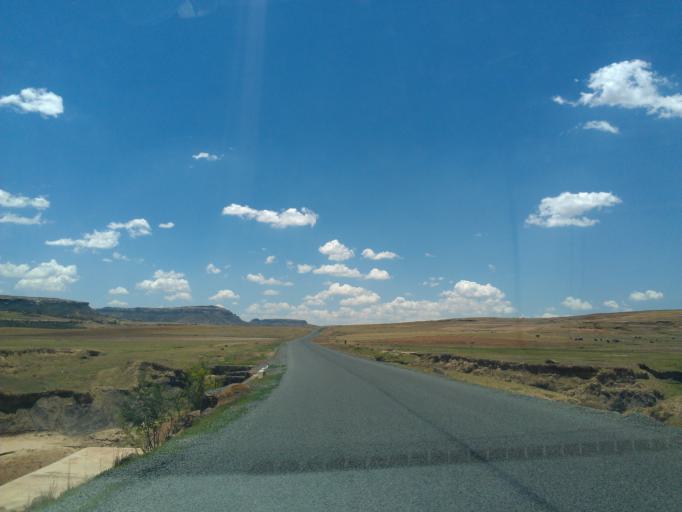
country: LS
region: Berea
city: Teyateyaneng
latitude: -29.0859
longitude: 27.8634
